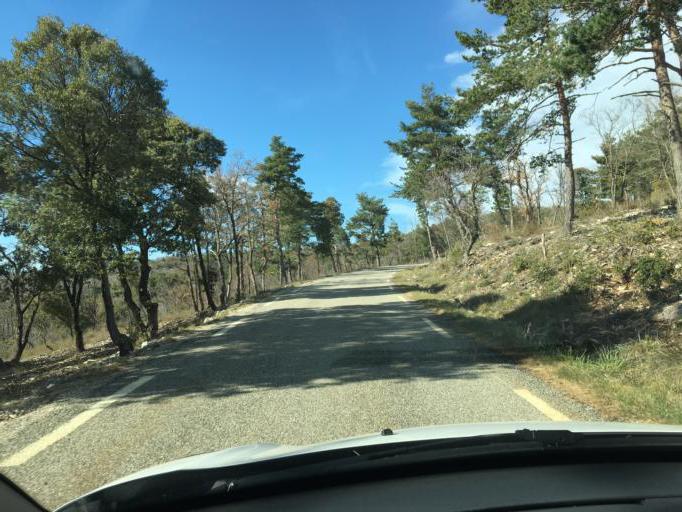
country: FR
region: Provence-Alpes-Cote d'Azur
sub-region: Departement du Vaucluse
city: Saint-Saturnin-les-Apt
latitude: 43.9661
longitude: 5.4621
